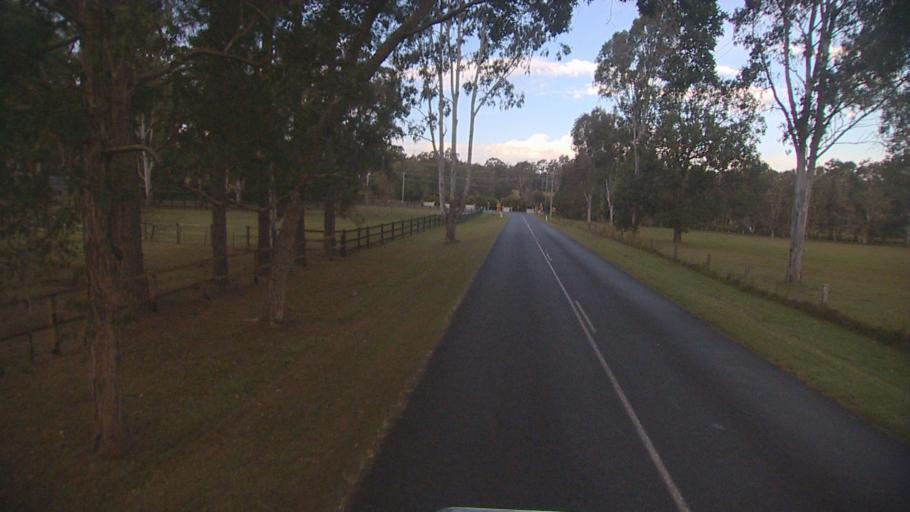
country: AU
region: Queensland
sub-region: Logan
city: Cedar Vale
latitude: -27.8396
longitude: 153.1035
